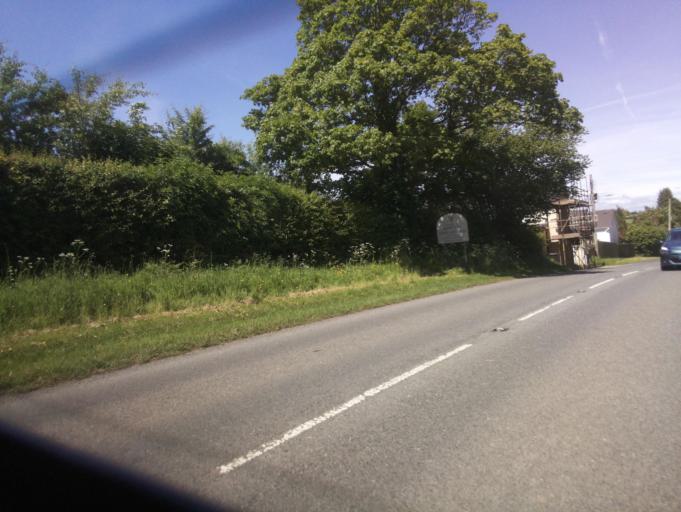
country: GB
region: England
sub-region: Devon
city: Newton Poppleford
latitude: 50.6943
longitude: -3.3063
